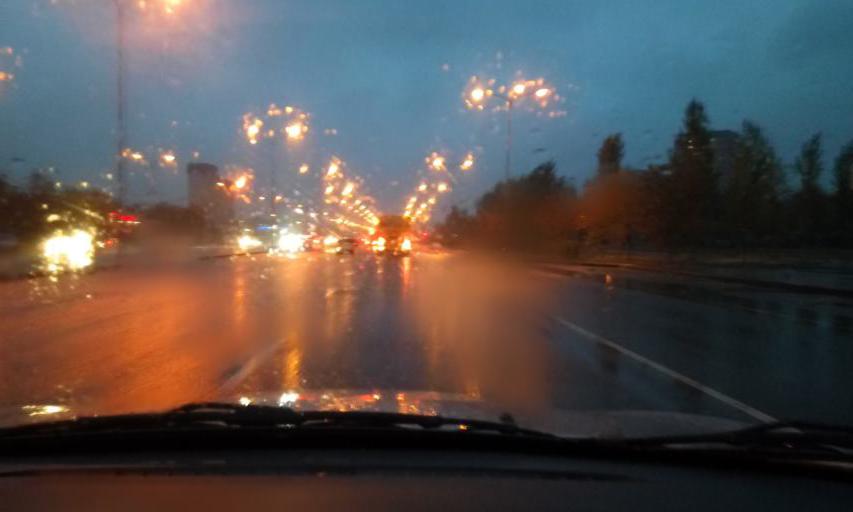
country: KZ
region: Astana Qalasy
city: Astana
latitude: 51.1824
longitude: 71.3697
